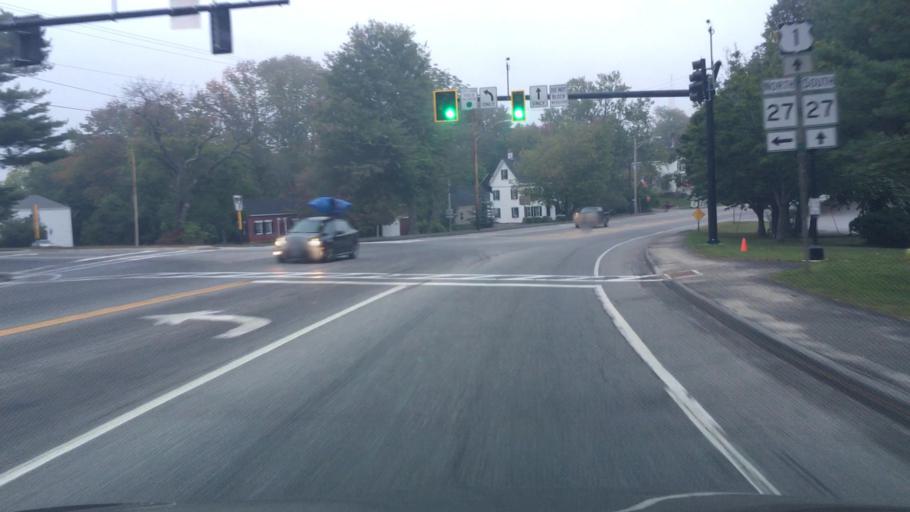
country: US
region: Maine
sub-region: Lincoln County
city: Wiscasset
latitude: 44.0049
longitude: -69.6700
